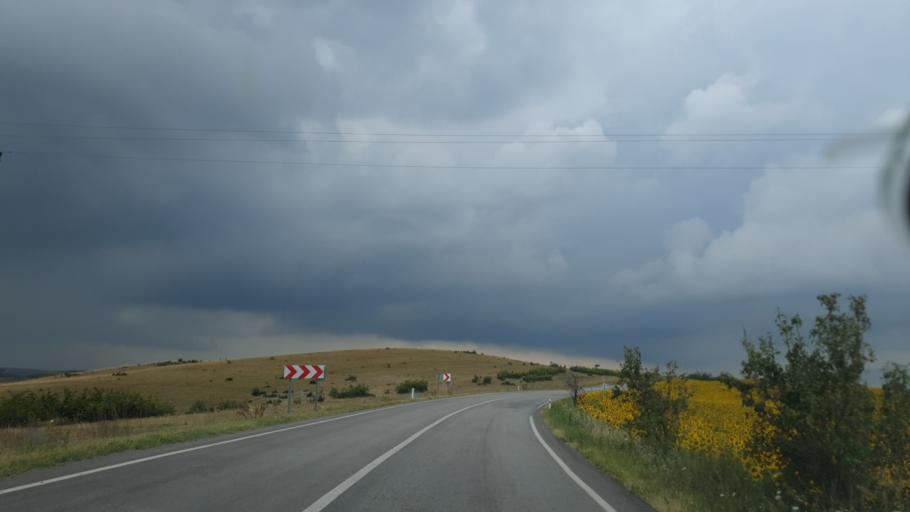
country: TR
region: Tekirdag
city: Hayrabolu
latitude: 41.2218
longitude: 27.0216
